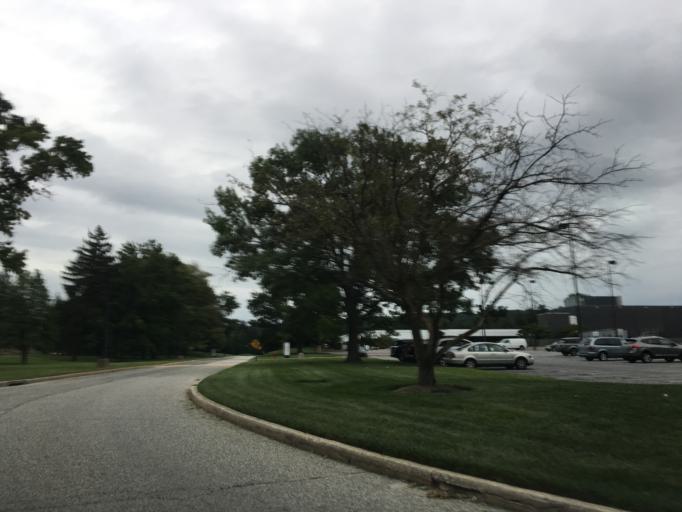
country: US
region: Maryland
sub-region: Baltimore County
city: Cockeysville
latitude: 39.4882
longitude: -76.6525
